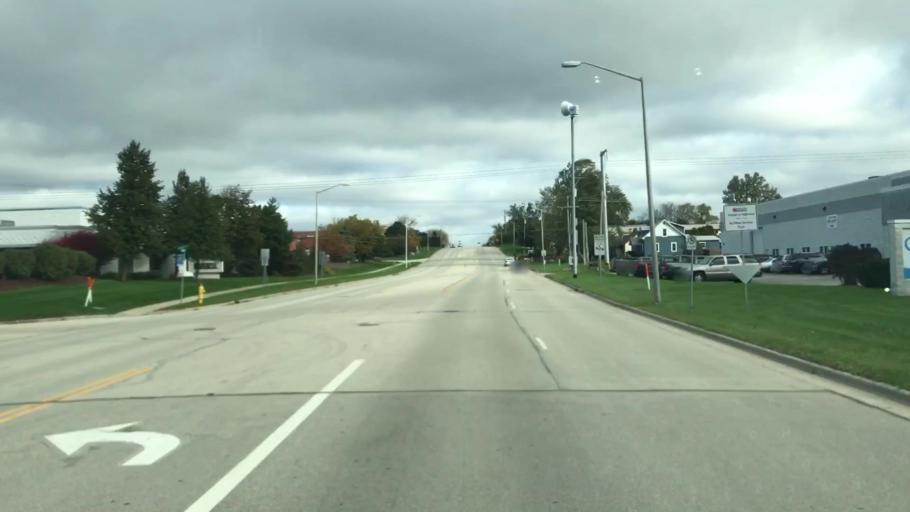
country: US
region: Wisconsin
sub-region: Waukesha County
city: Waukesha
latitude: 43.0275
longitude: -88.2259
